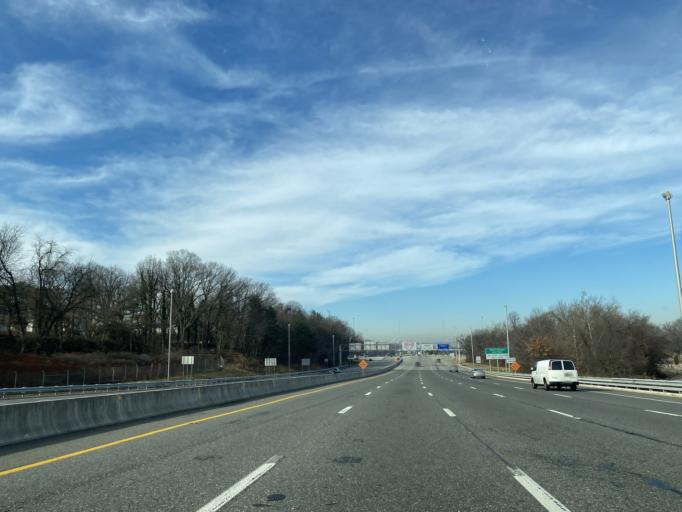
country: US
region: New Jersey
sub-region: Camden County
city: Pennsauken
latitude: 39.9744
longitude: -75.0438
